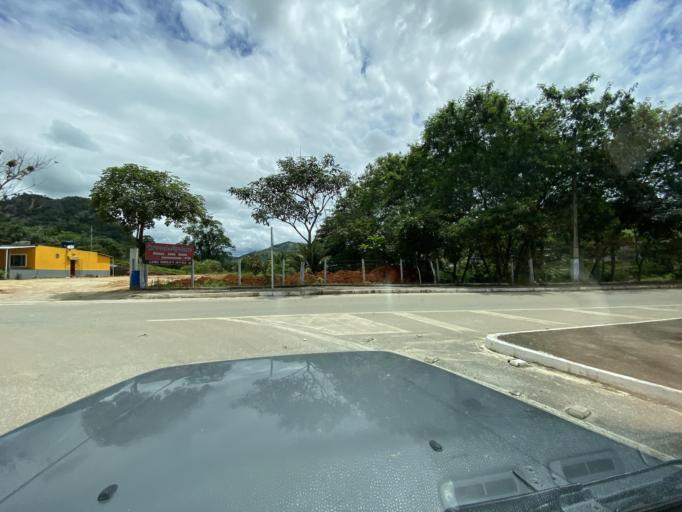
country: BR
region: Espirito Santo
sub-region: Jeronimo Monteiro
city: Jeronimo Monteiro
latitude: -20.7959
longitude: -41.4041
